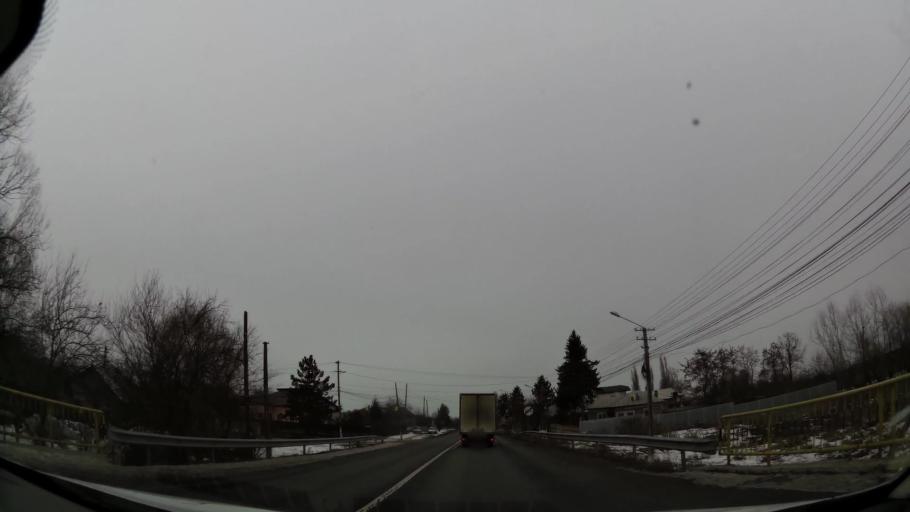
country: RO
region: Dambovita
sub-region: Comuna Racari
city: Racari
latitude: 44.6291
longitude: 25.7330
